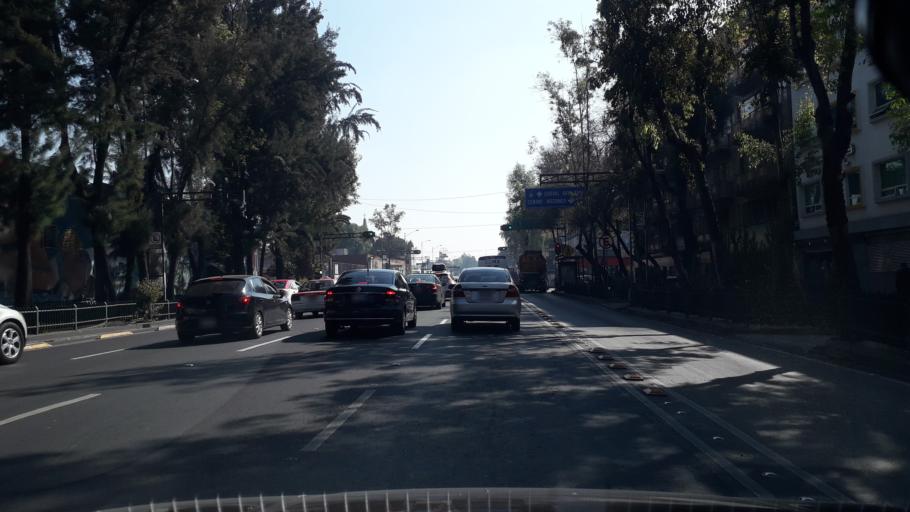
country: MX
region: Mexico City
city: Cuauhtemoc
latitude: 19.4455
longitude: -99.1483
